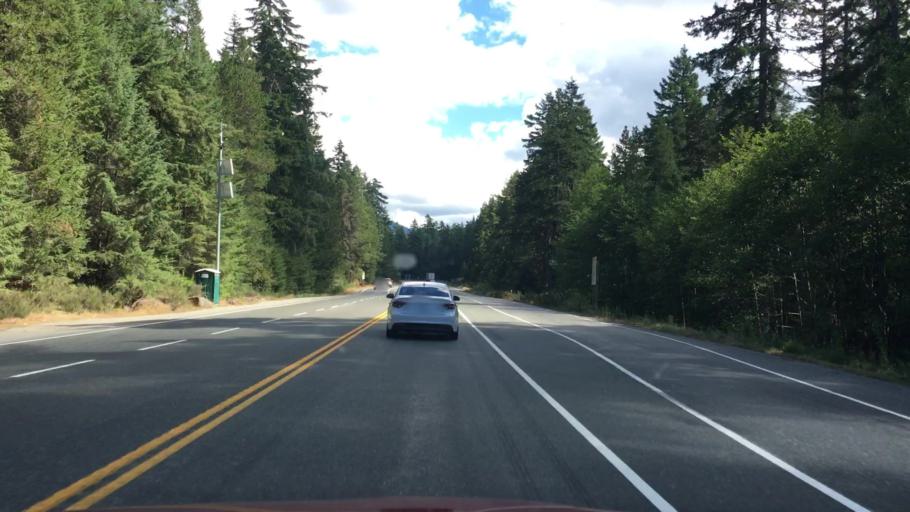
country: CA
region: British Columbia
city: Port Alberni
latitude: 49.2480
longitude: -124.6919
